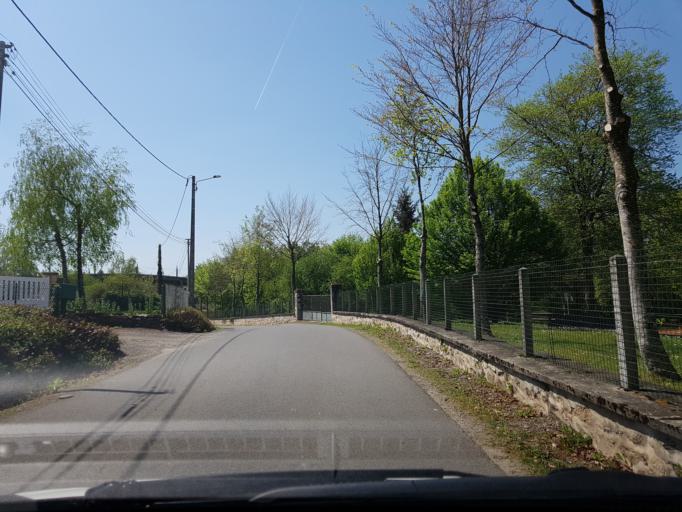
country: FR
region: Limousin
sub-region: Departement de la Haute-Vienne
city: Saint-Junien
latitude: 45.9017
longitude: 0.9036
